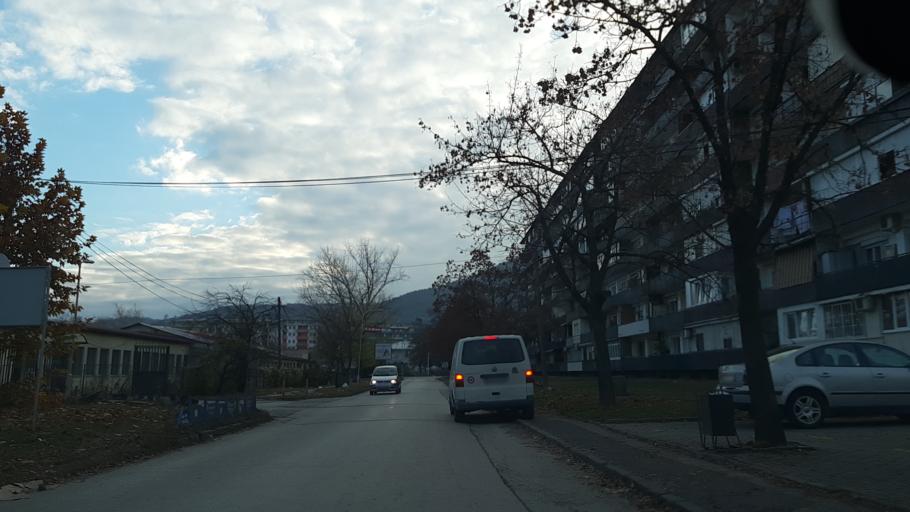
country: MK
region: Kisela Voda
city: Usje
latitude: 41.9796
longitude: 21.4479
